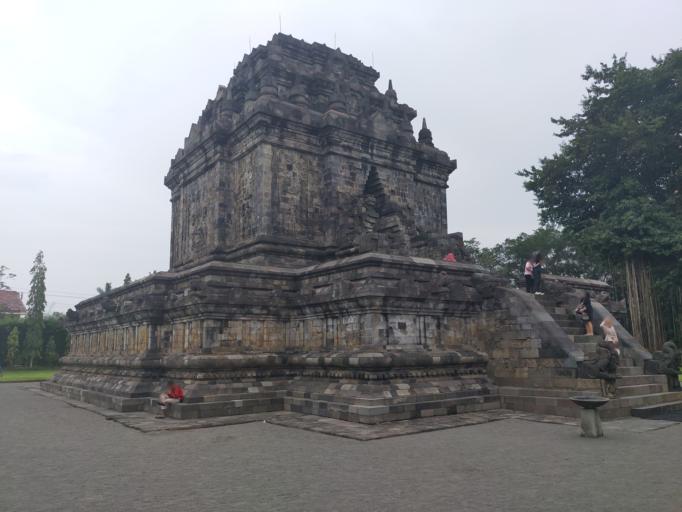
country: ID
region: Central Java
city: Muntilan
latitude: -7.6046
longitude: 110.2300
